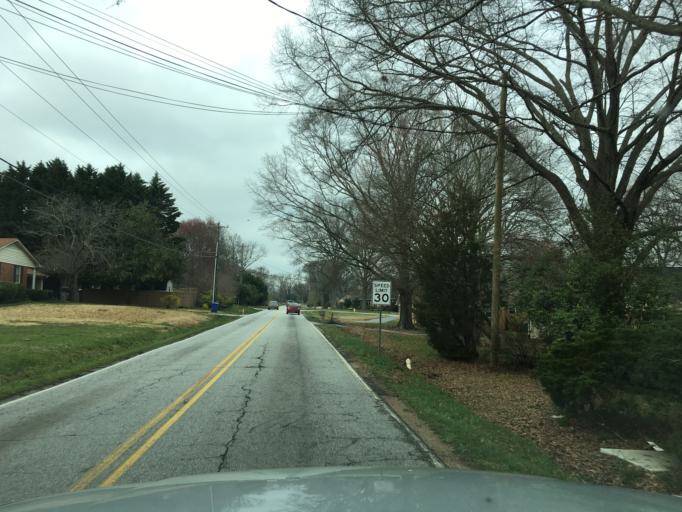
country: US
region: South Carolina
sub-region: Greenville County
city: Wade Hampton
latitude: 34.8804
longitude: -82.3298
